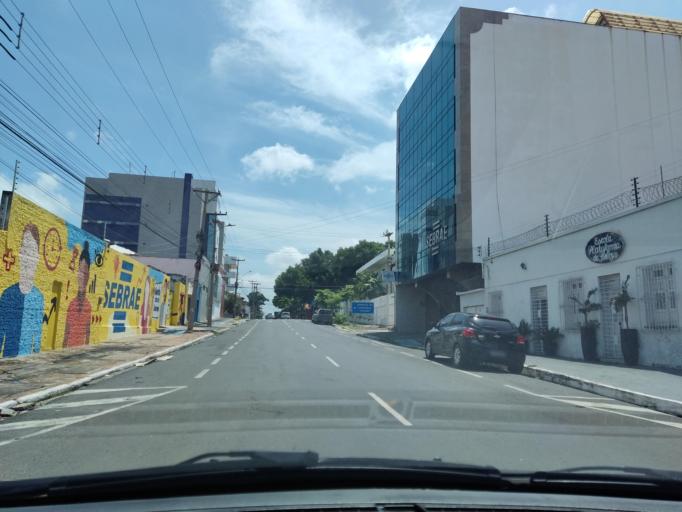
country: BR
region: Piaui
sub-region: Teresina
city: Teresina
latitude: -5.0859
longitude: -42.8188
